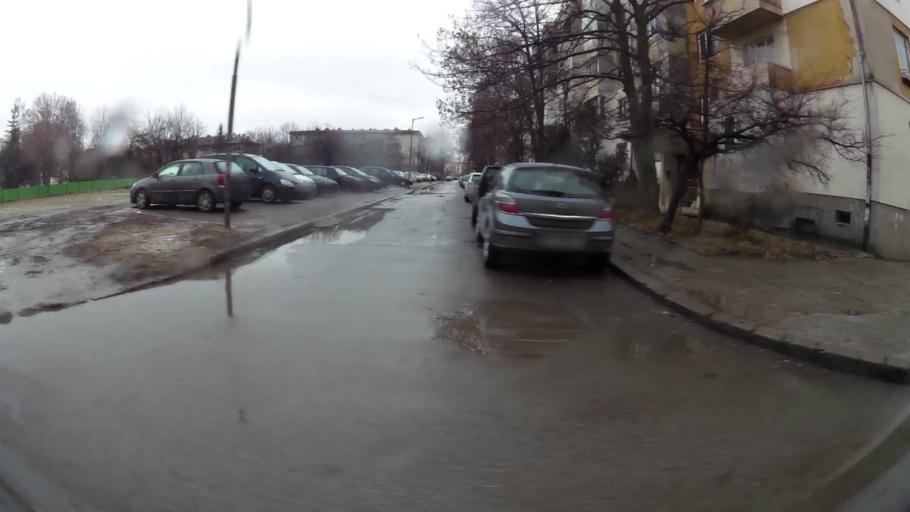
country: BG
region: Sofia-Capital
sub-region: Stolichna Obshtina
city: Sofia
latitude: 42.6641
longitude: 23.3953
